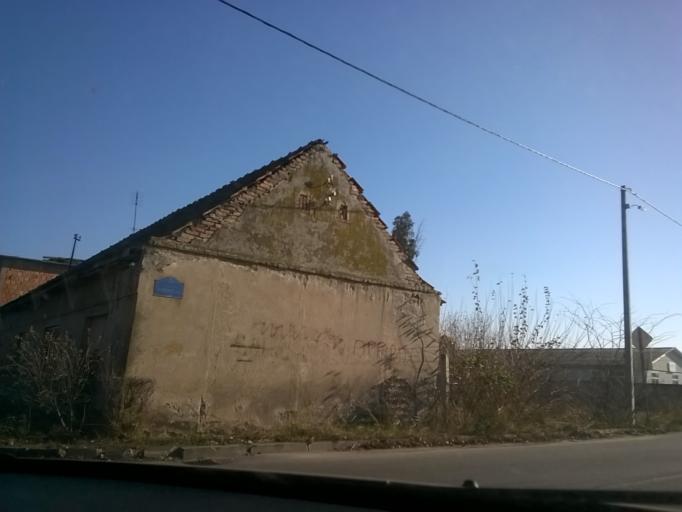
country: RS
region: Autonomna Pokrajina Vojvodina
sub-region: Juznobanatski Okrug
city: Vrsac
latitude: 45.1129
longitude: 21.2769
